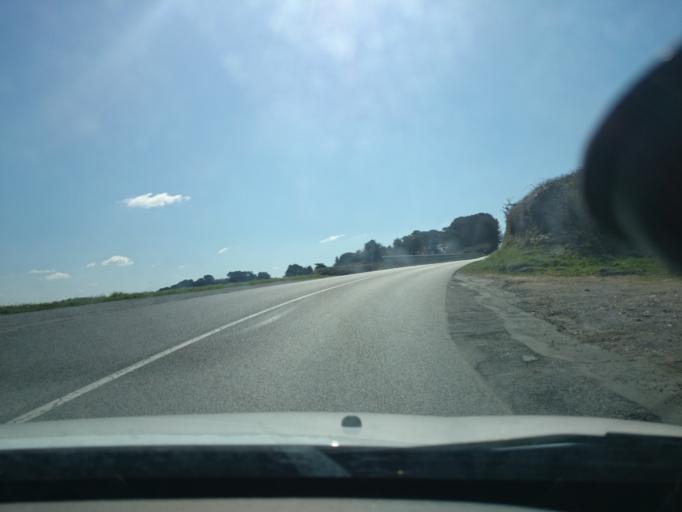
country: FR
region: Brittany
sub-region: Departement des Cotes-d'Armor
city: Tregastel
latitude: 48.8266
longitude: -3.4724
